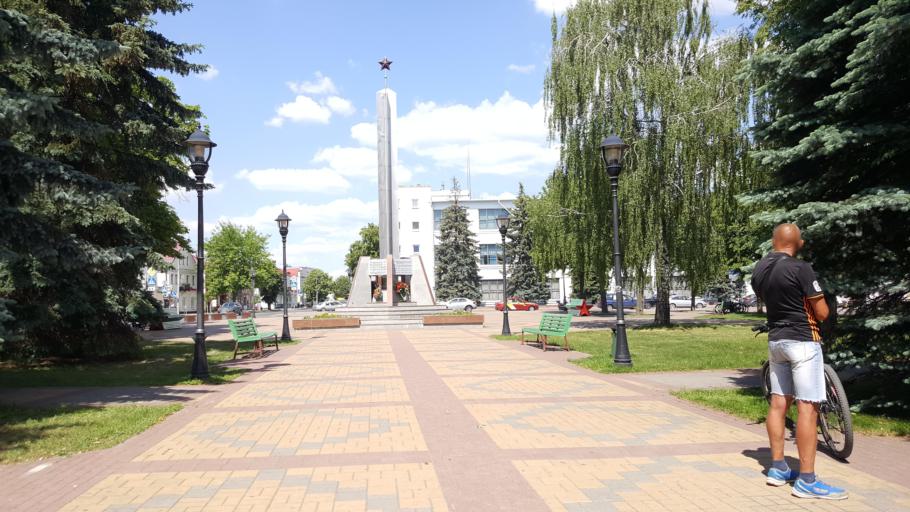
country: BY
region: Brest
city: Kobryn
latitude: 52.2111
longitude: 24.3562
